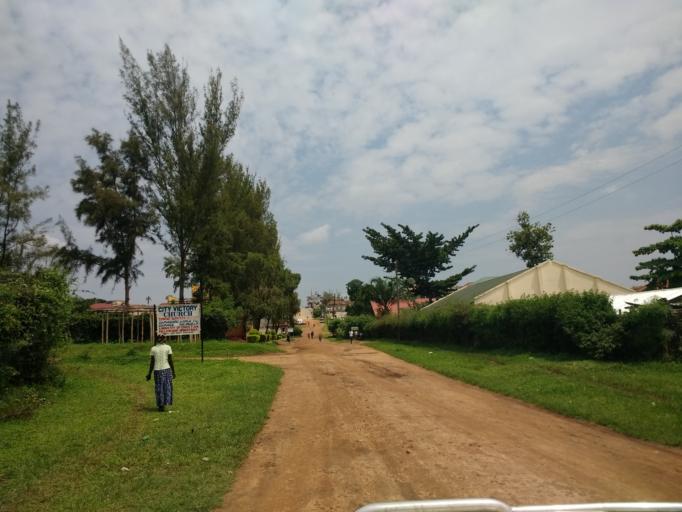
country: UG
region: Eastern Region
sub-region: Mbale District
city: Mbale
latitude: 1.0760
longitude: 34.1826
